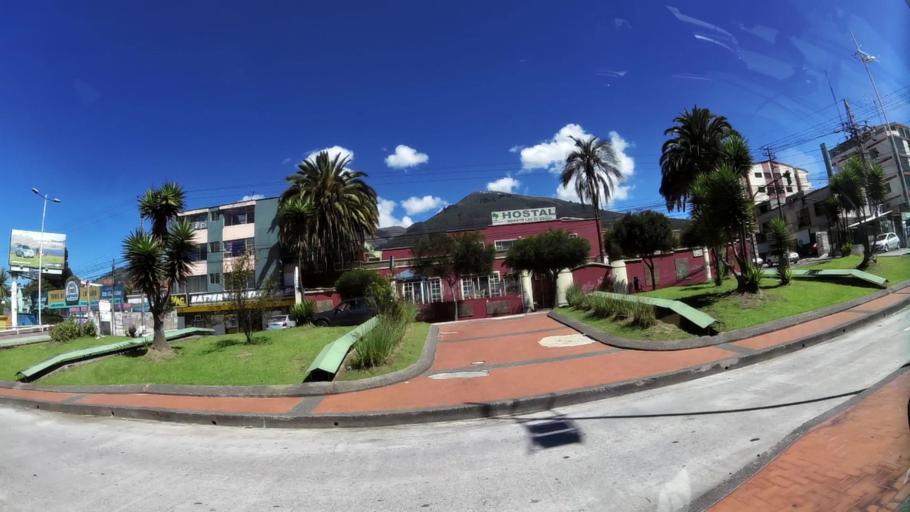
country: EC
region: Pichincha
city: Quito
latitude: -0.1770
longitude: -78.4939
